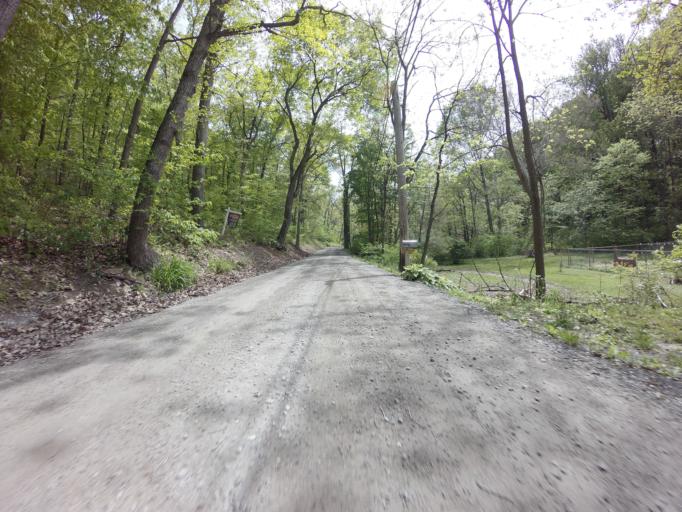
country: US
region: Maryland
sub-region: Carroll County
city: New Windsor
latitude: 39.4947
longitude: -77.1080
